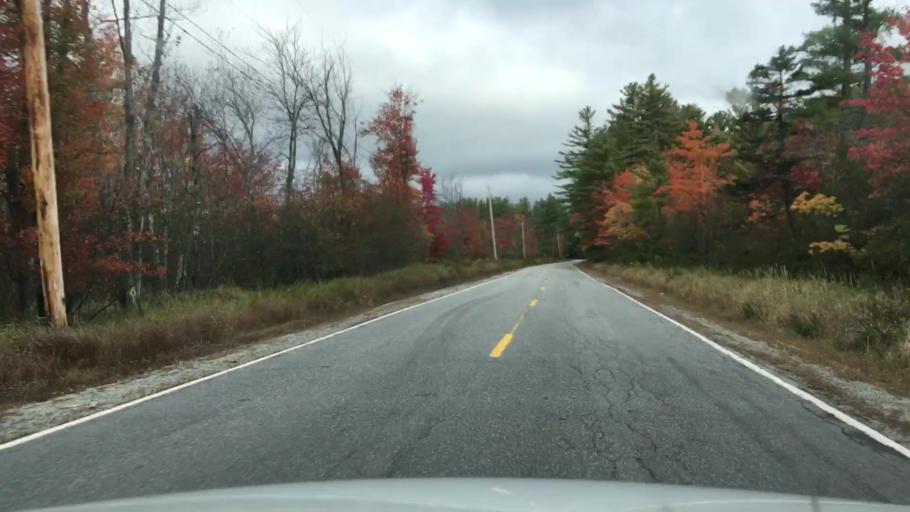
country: US
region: Maine
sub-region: Oxford County
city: Bethel
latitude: 44.3280
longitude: -70.7723
